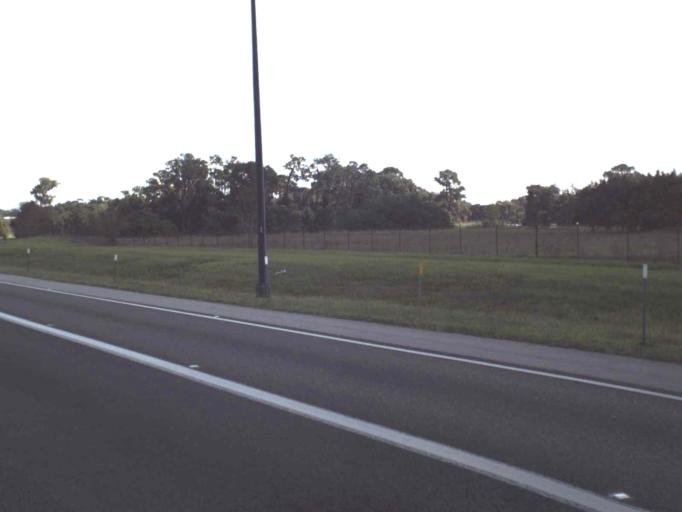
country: US
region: Florida
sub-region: Polk County
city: Crystal Lake
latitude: 27.9981
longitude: -81.9078
